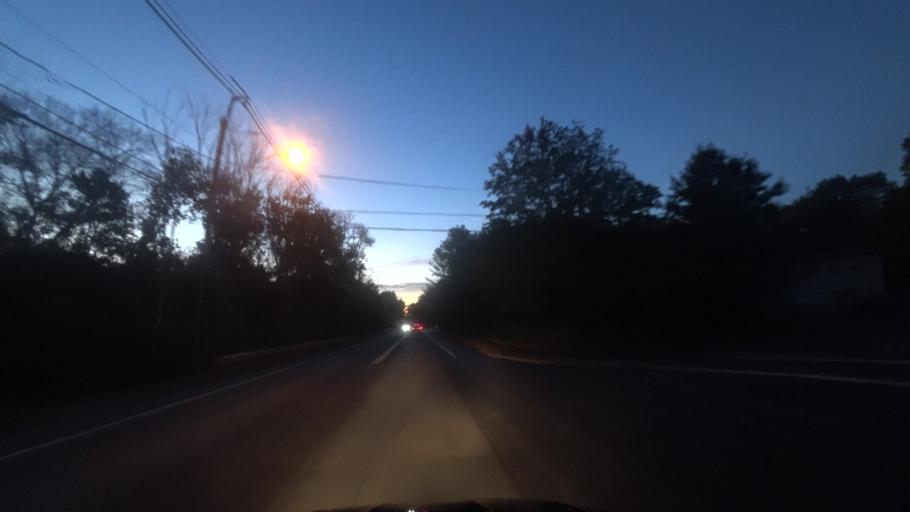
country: US
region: Massachusetts
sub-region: Middlesex County
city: Reading
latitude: 42.5495
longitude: -71.0950
